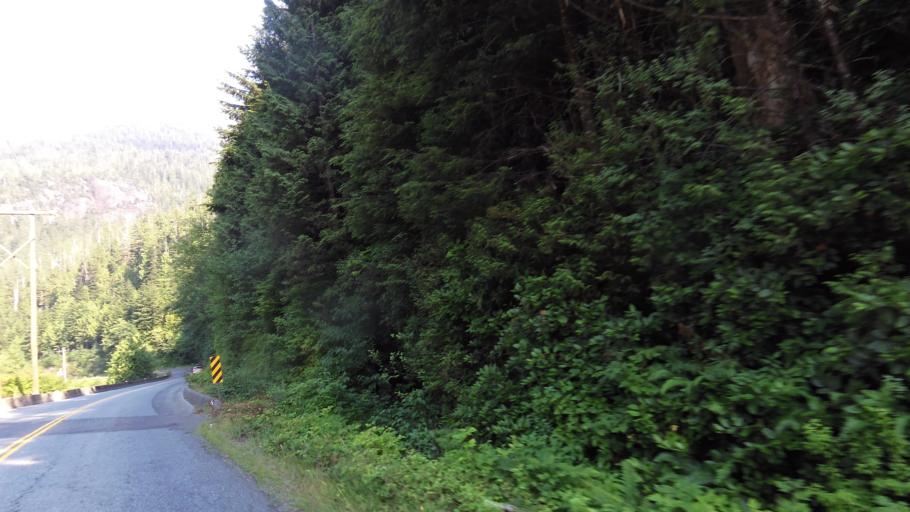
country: CA
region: British Columbia
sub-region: Regional District of Alberni-Clayoquot
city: Ucluelet
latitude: 49.1212
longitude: -125.4311
